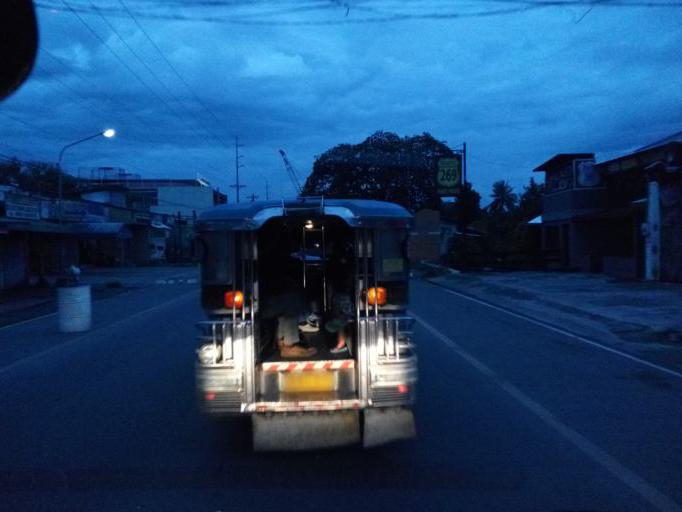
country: PH
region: Cagayan Valley
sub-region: Province of Nueva Vizcaya
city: Solano
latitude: 16.5103
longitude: 121.1769
